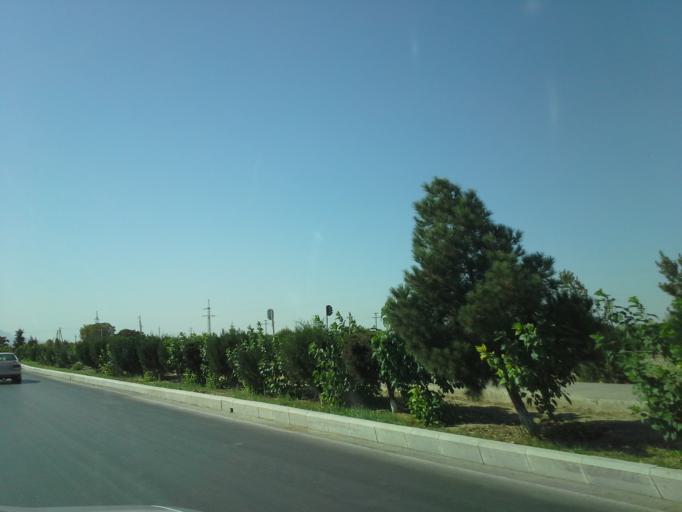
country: TM
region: Ahal
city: Annau
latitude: 37.9160
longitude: 58.4724
